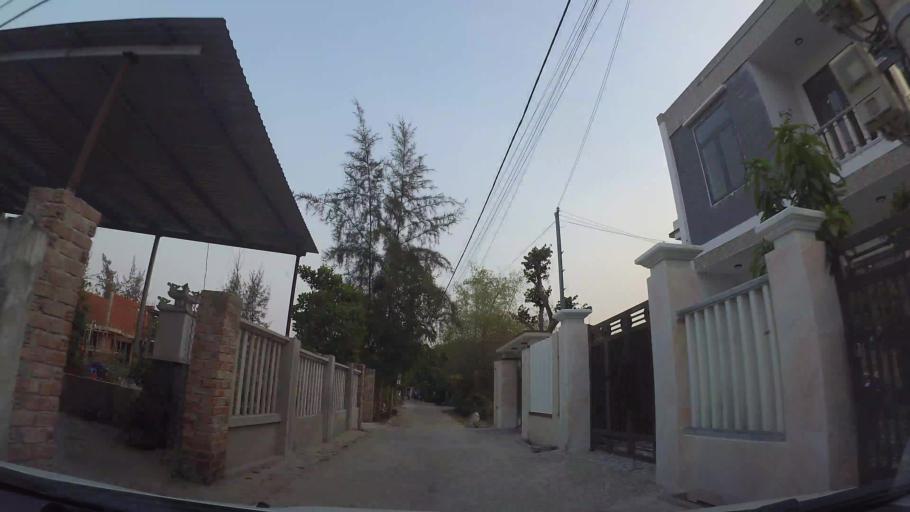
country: VN
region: Da Nang
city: Ngu Hanh Son
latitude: 15.9771
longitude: 108.2396
